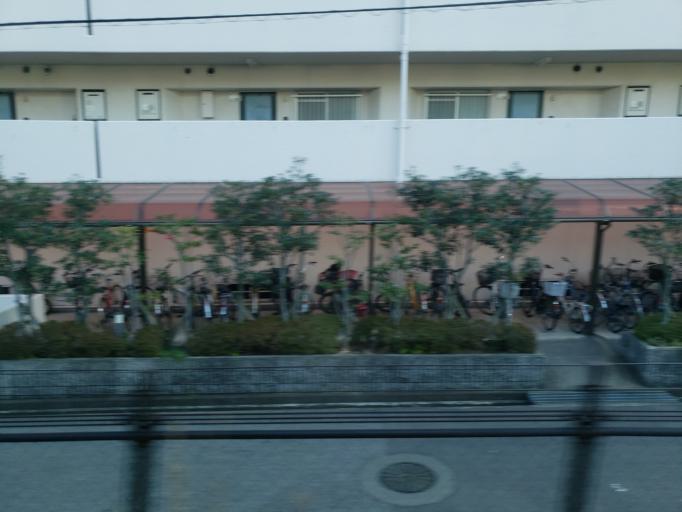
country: JP
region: Hyogo
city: Ashiya
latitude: 34.7278
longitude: 135.2823
